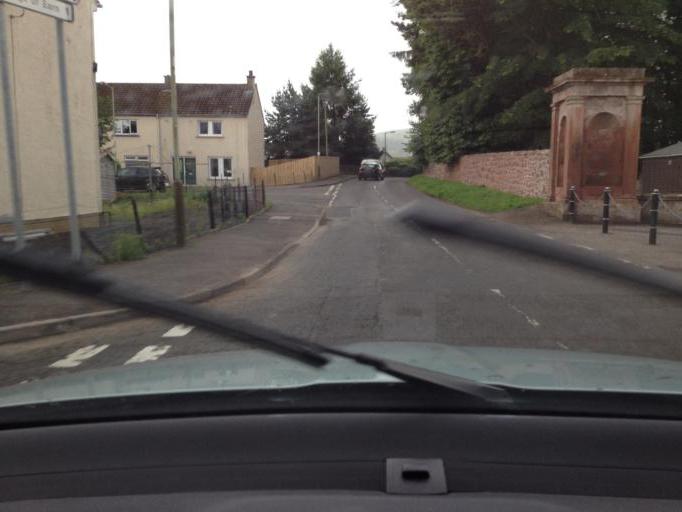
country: GB
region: Scotland
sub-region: Perth and Kinross
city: Bridge of Earn
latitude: 56.3412
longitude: -3.4099
